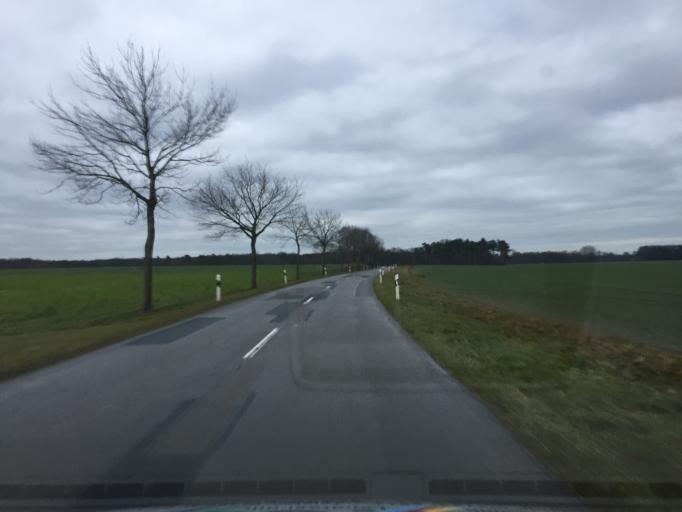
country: DE
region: Lower Saxony
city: Borstel
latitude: 52.6556
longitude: 8.9867
